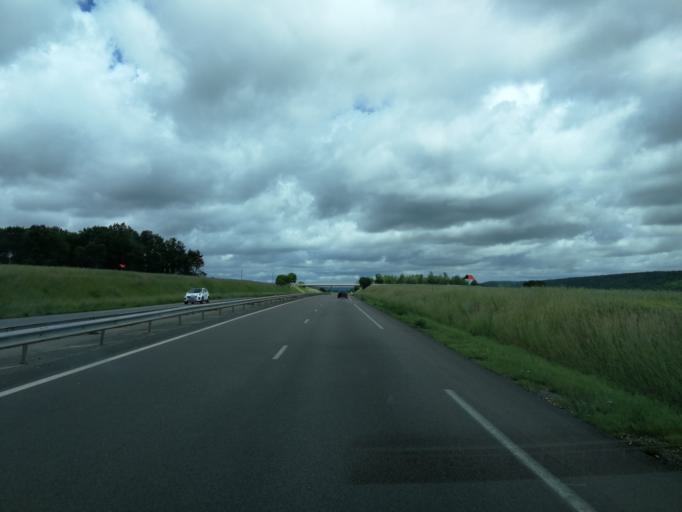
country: FR
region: Haute-Normandie
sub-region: Departement de l'Eure
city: Heudreville-sur-Eure
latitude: 49.1292
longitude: 1.1836
